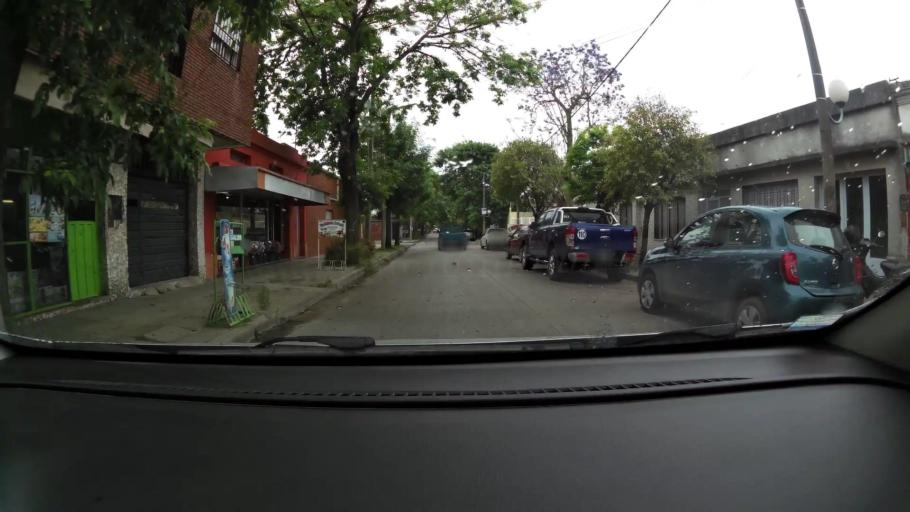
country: AR
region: Buenos Aires
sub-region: Partido de Zarate
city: Zarate
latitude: -34.0905
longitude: -59.0289
